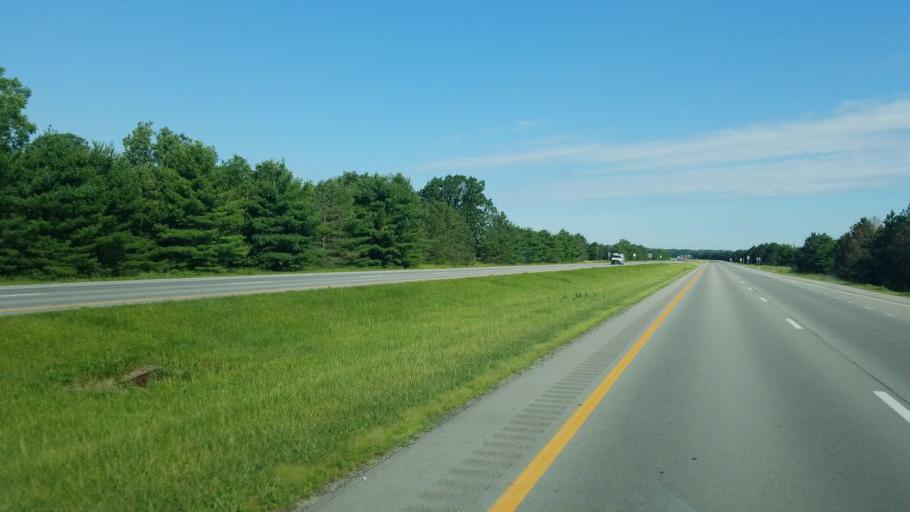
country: US
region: Ohio
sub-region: Wyandot County
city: Carey
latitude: 40.9738
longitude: -83.4888
